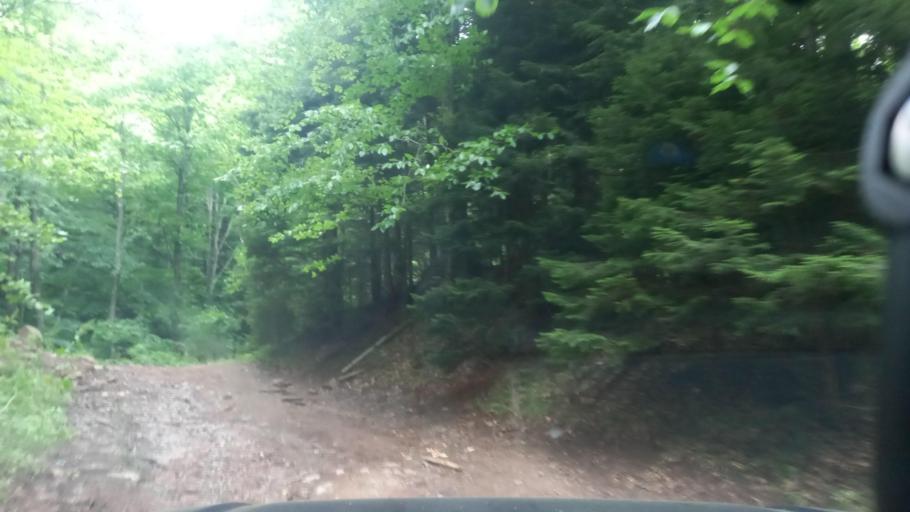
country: RU
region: Karachayevo-Cherkesiya
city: Kurdzhinovo
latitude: 43.8141
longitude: 40.8802
